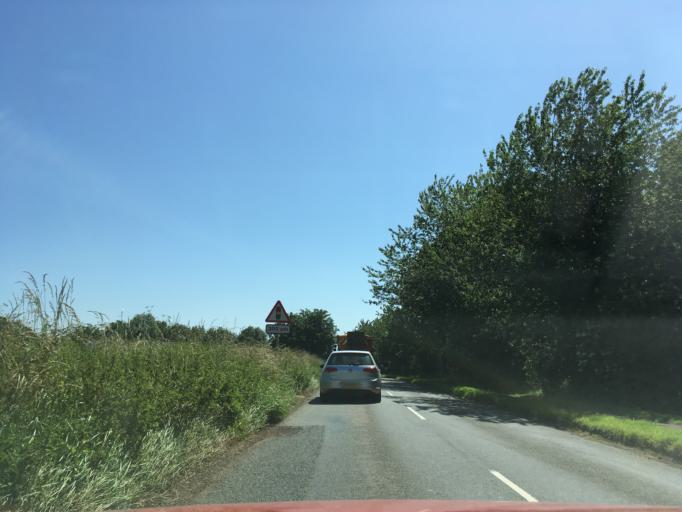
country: GB
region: England
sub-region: Oxfordshire
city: Deddington
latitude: 51.9828
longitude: -1.3335
